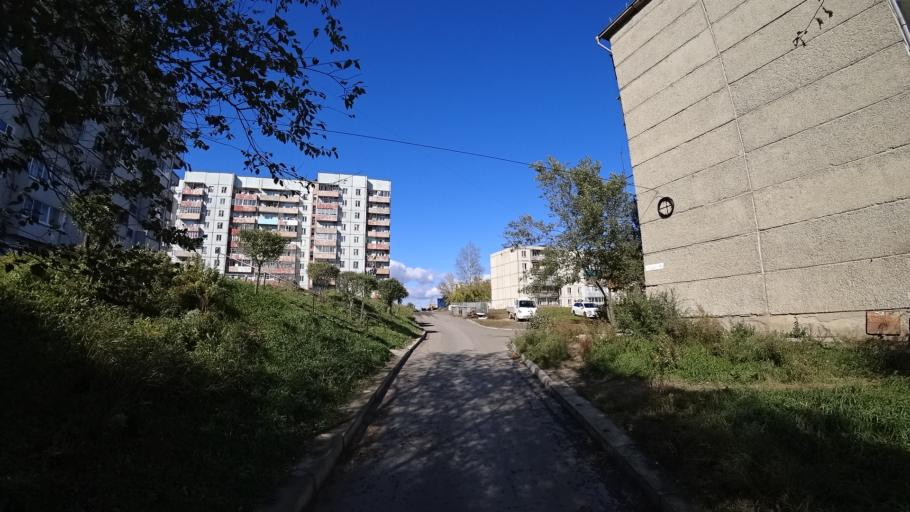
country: RU
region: Khabarovsk Krai
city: Amursk
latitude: 50.2416
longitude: 136.9051
